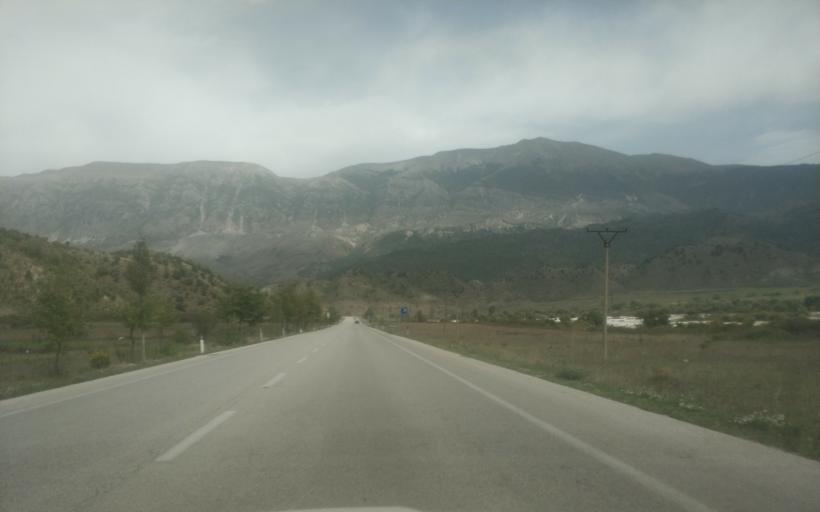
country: AL
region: Gjirokaster
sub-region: Rrethi i Gjirokastres
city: Picar
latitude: 40.1976
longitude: 20.0852
